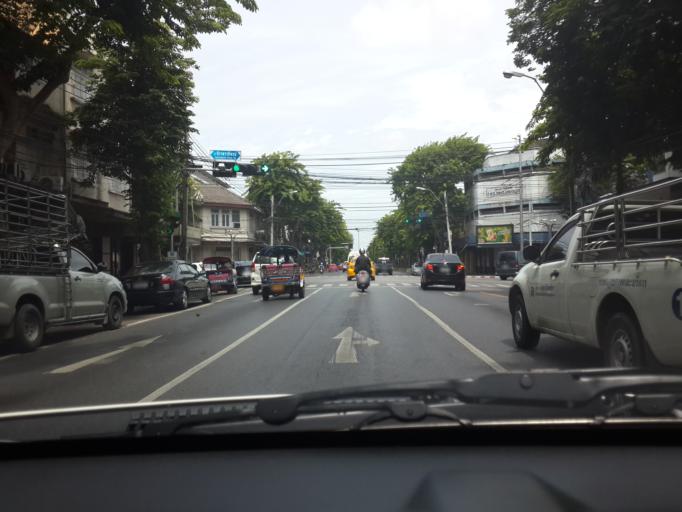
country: TH
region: Bangkok
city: Pom Prap Sattru Phai
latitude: 13.7565
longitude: 100.5101
